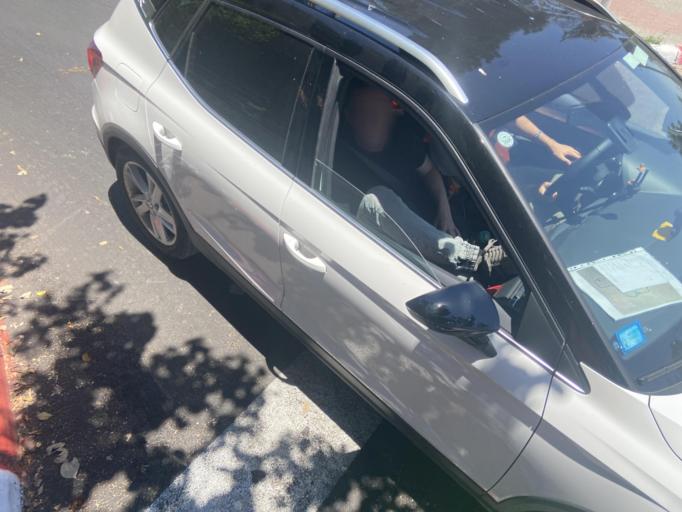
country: IL
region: Tel Aviv
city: Or Yehuda
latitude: 32.0301
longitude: 34.8705
